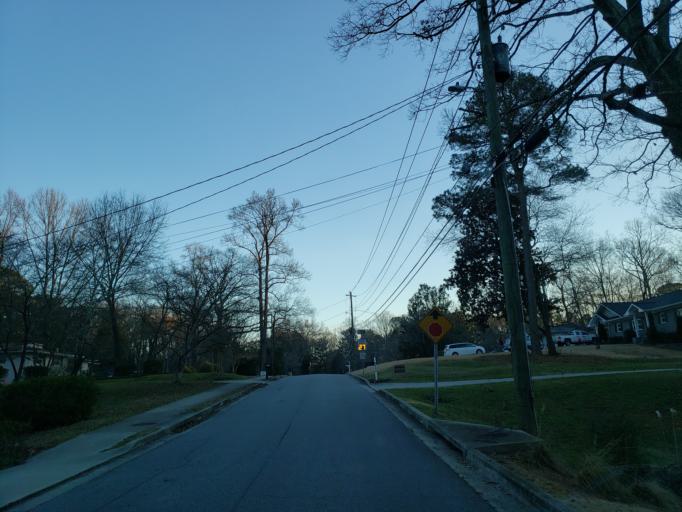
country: US
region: Georgia
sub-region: Cobb County
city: Smyrna
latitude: 33.8706
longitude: -84.5158
